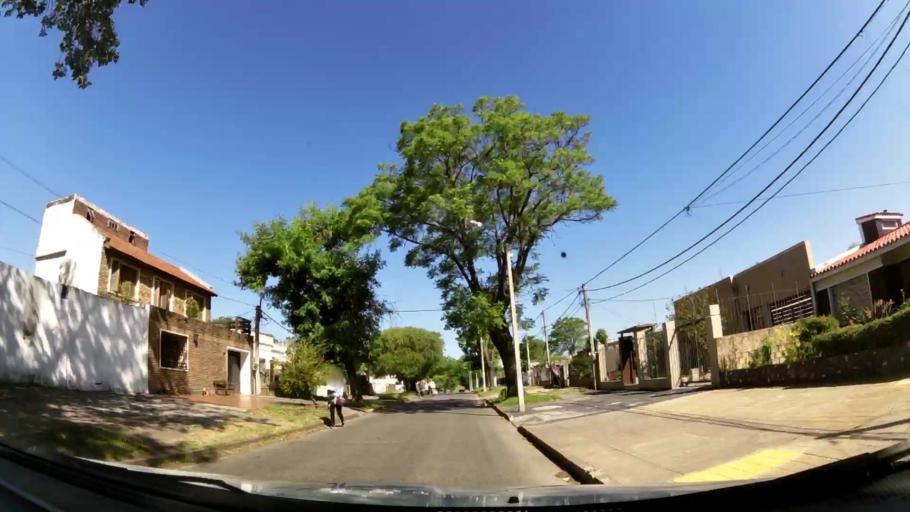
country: UY
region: Montevideo
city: Montevideo
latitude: -34.8560
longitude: -56.2376
